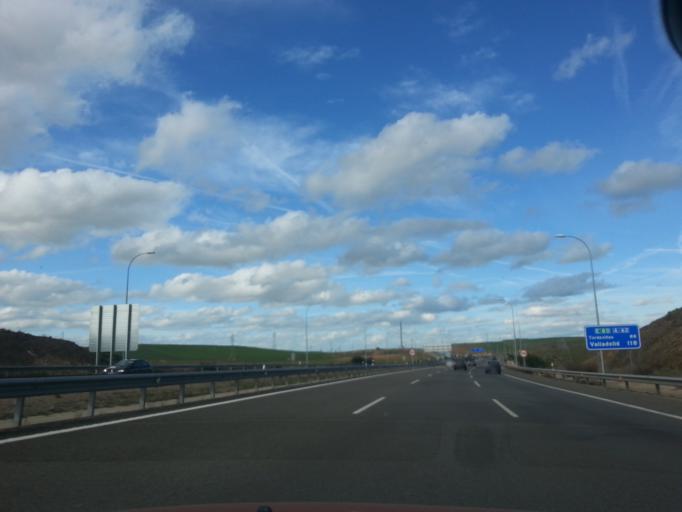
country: ES
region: Castille and Leon
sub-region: Provincia de Salamanca
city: Villamayor
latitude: 40.9683
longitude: -5.6979
